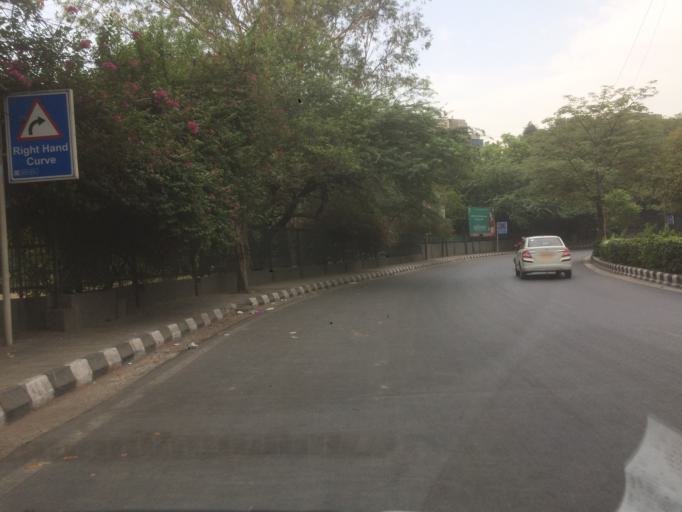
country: IN
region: NCT
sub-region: Central Delhi
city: Karol Bagh
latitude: 28.5726
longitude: 77.1740
